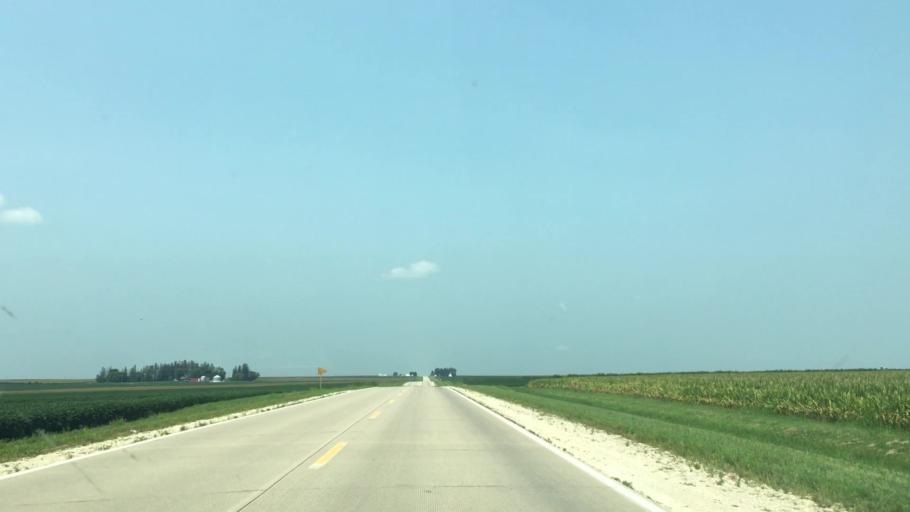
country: US
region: Iowa
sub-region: Fayette County
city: Oelwein
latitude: 42.6917
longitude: -91.8051
